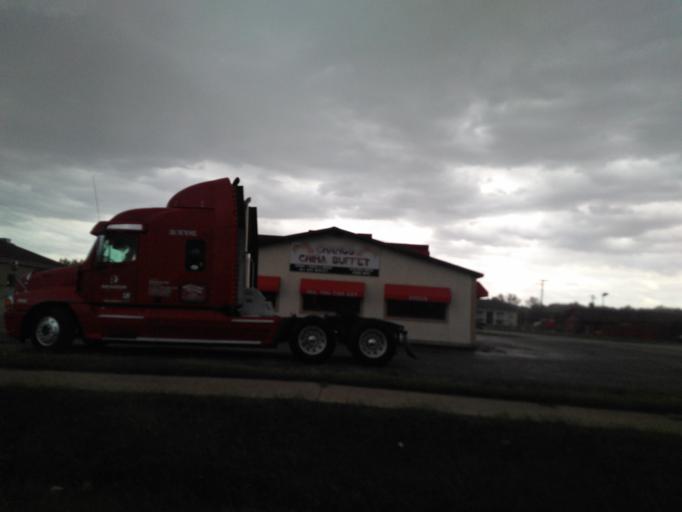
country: US
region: Illinois
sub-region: Bond County
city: Greenville
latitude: 38.8793
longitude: -89.3906
